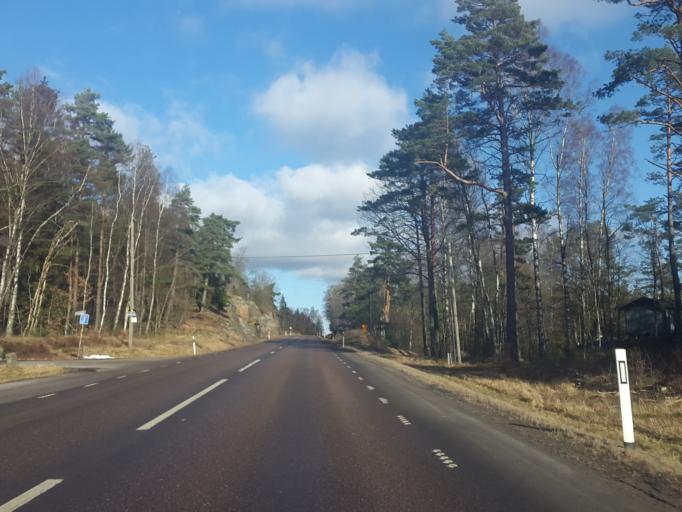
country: SE
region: Vaestra Goetaland
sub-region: Lerums Kommun
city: Grabo
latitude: 57.8524
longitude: 12.3103
